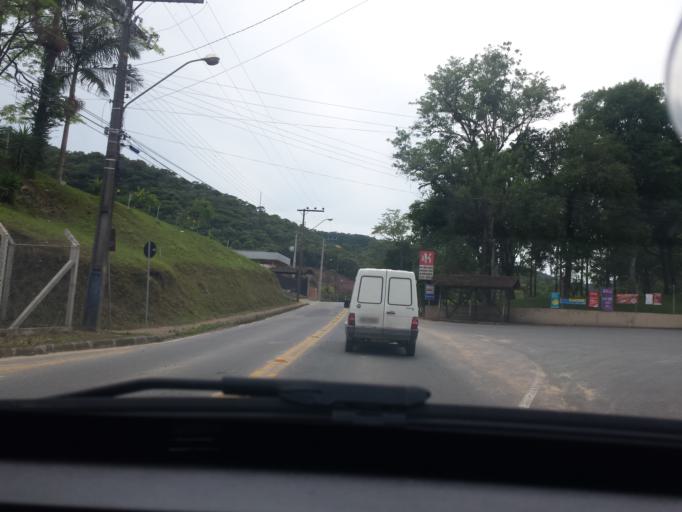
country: BR
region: Santa Catarina
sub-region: Gaspar
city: Gaspar
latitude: -26.8897
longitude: -48.9956
